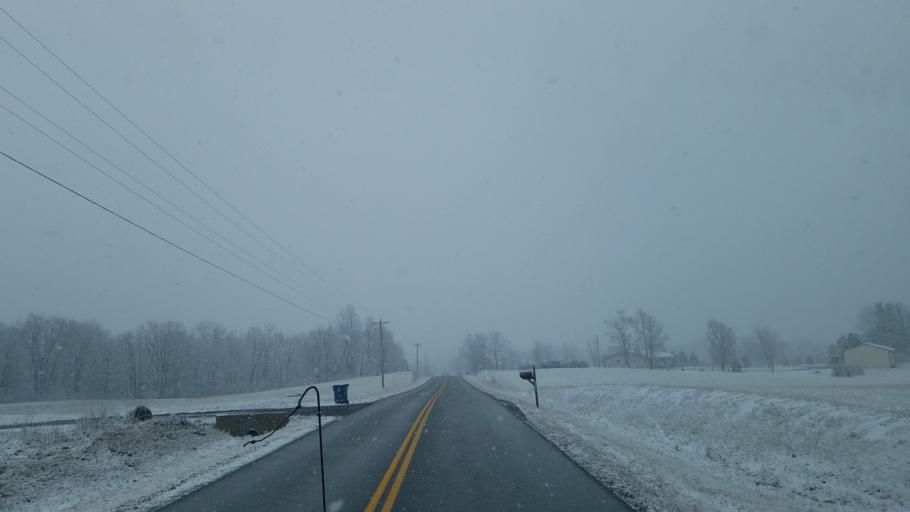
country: US
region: Ohio
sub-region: Champaign County
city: North Lewisburg
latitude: 40.3401
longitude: -83.6178
